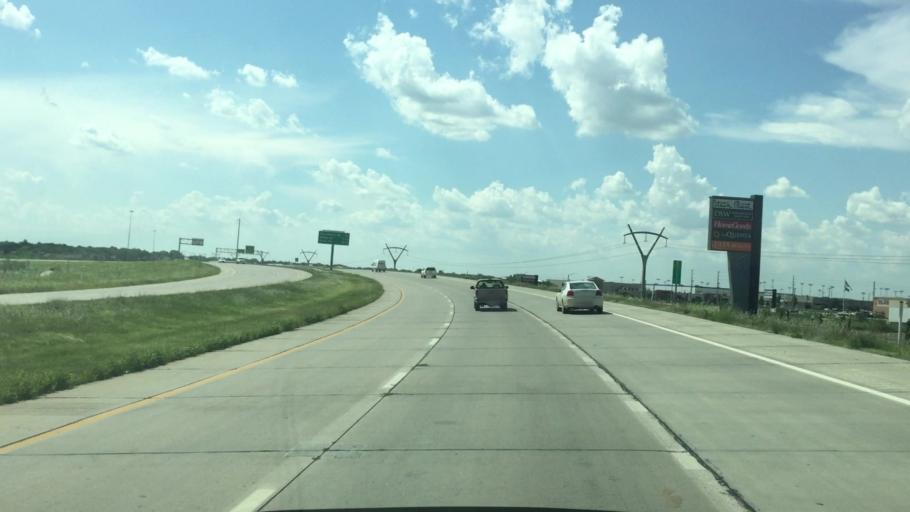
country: US
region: Kansas
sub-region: Butler County
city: Andover
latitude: 37.7295
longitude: -97.2034
